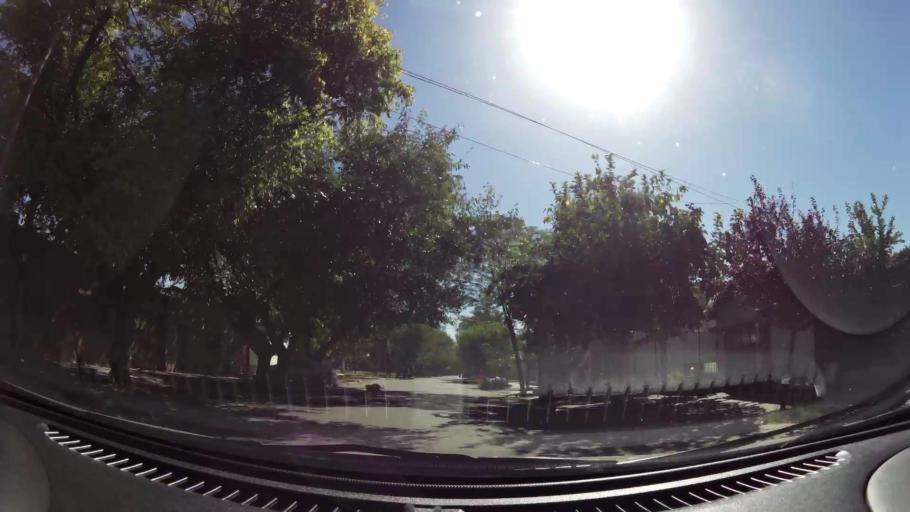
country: AR
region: Mendoza
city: Mendoza
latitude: -32.8817
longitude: -68.8087
